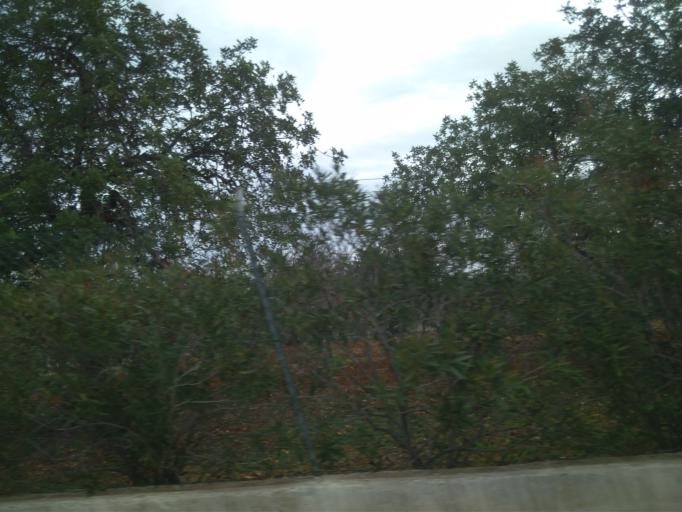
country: PT
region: Faro
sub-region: Faro
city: Santa Barbara de Nexe
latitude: 37.0789
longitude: -7.9593
